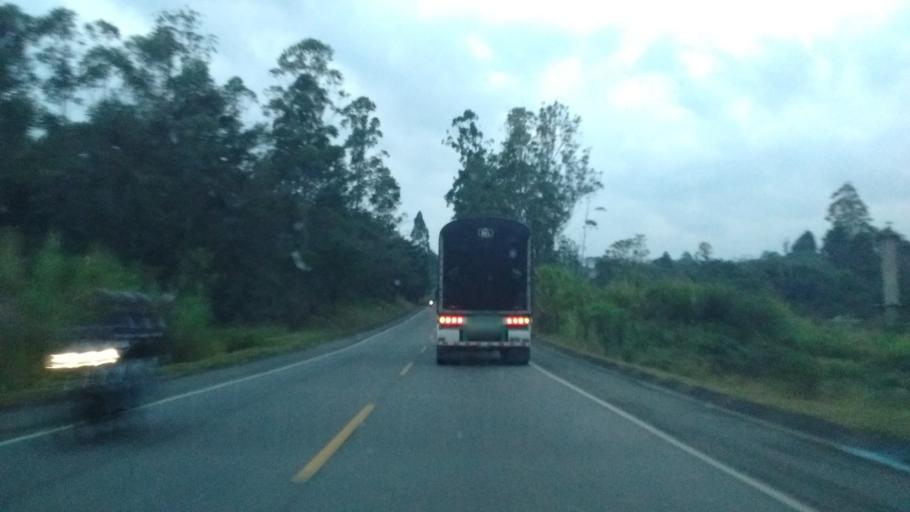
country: CO
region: Cauca
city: Popayan
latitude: 2.3858
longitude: -76.6660
